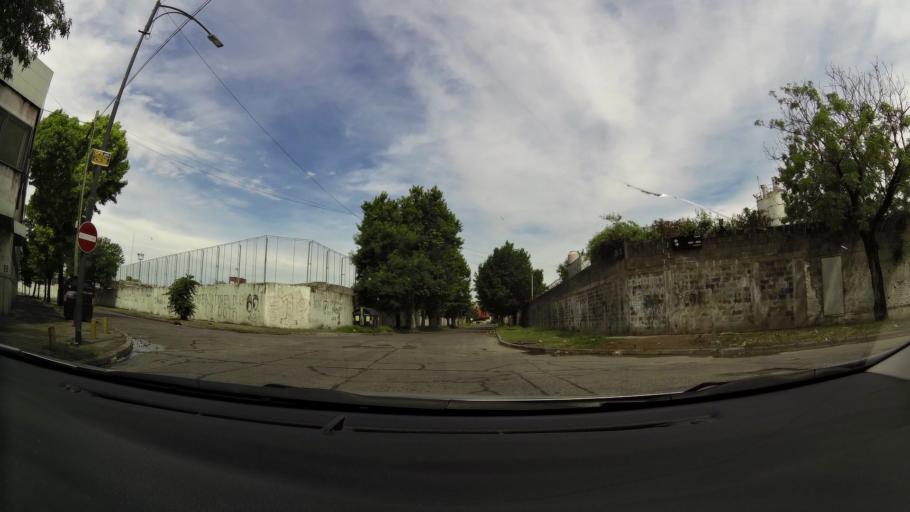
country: AR
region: Buenos Aires
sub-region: Partido de Lanus
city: Lanus
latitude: -34.6576
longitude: -58.4202
